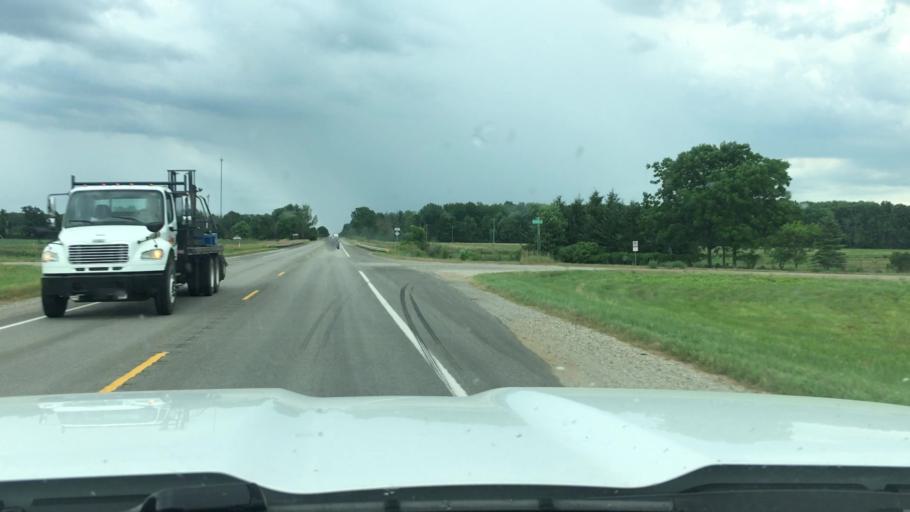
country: US
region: Michigan
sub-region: Montcalm County
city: Carson City
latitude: 43.1767
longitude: -84.8183
